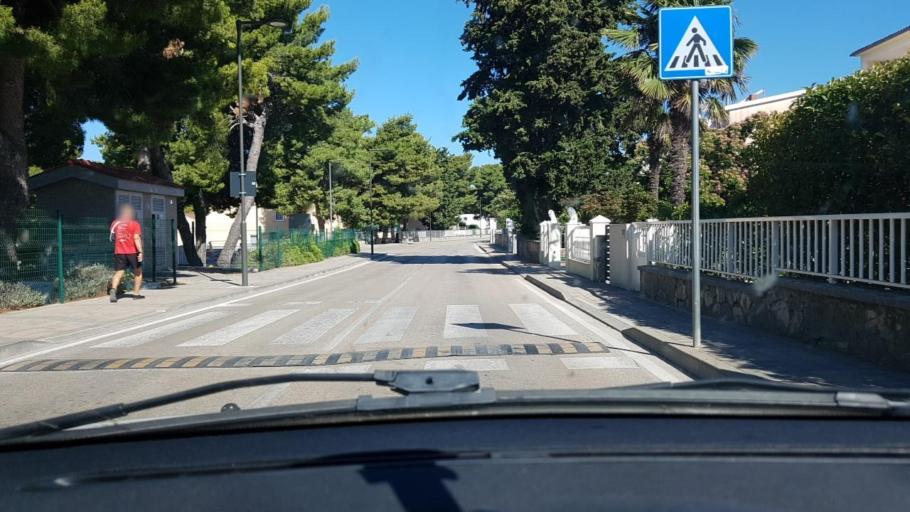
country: HR
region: Sibensko-Kniniska
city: Vodice
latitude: 43.7568
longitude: 15.7860
